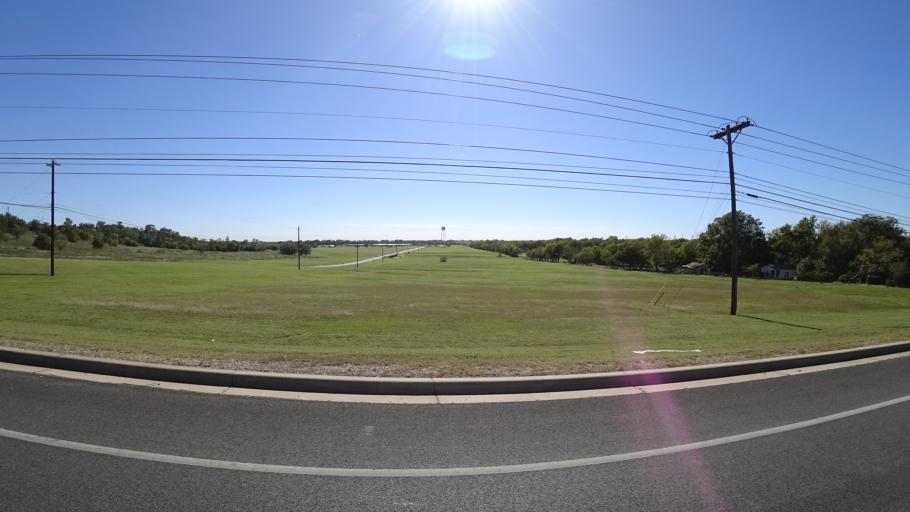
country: US
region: Texas
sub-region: Travis County
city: Hornsby Bend
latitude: 30.2787
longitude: -97.6425
